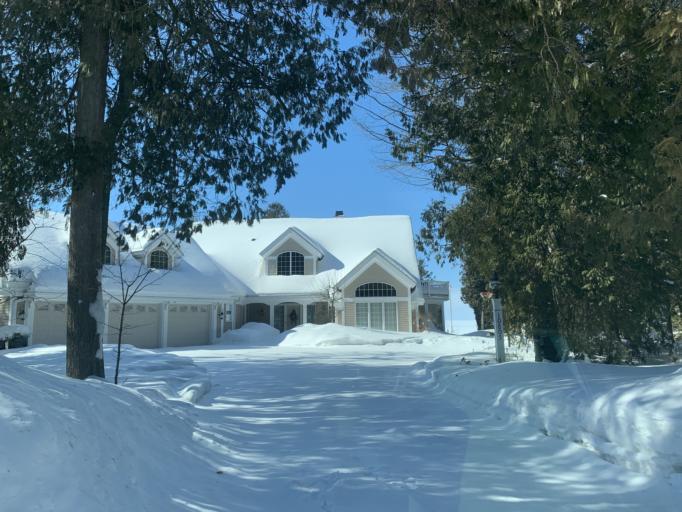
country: US
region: Wisconsin
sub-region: Door County
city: Sturgeon Bay
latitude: 45.1955
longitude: -87.1188
